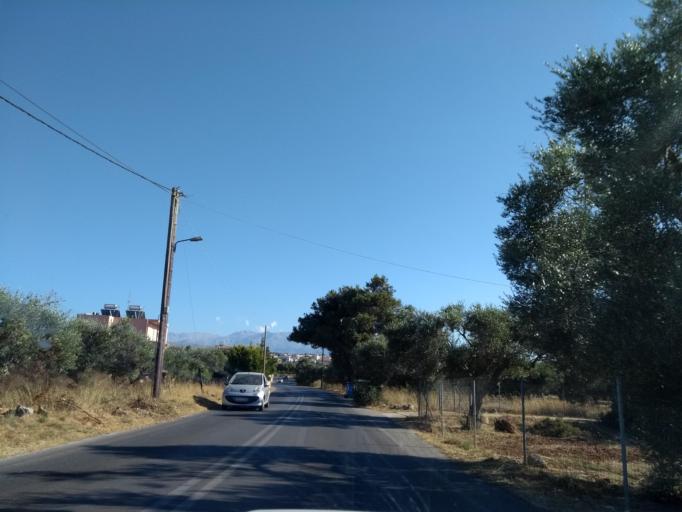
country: GR
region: Crete
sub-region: Nomos Chanias
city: Pithari
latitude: 35.5429
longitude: 24.0821
